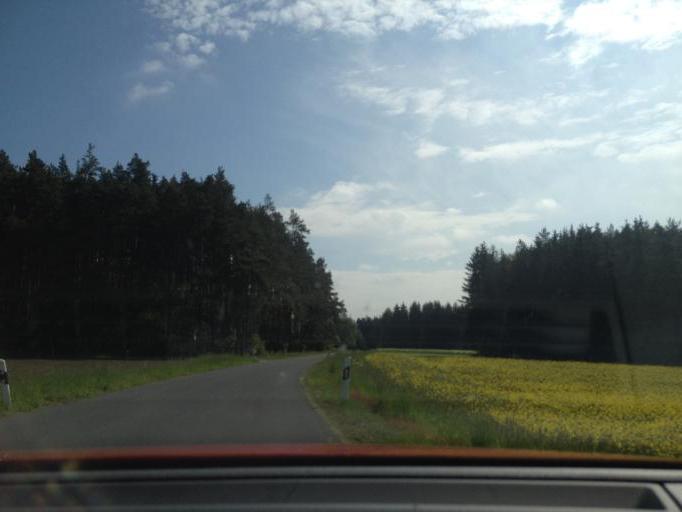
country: DE
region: Bavaria
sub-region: Upper Franconia
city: Marktredwitz
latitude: 50.0285
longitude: 12.1234
